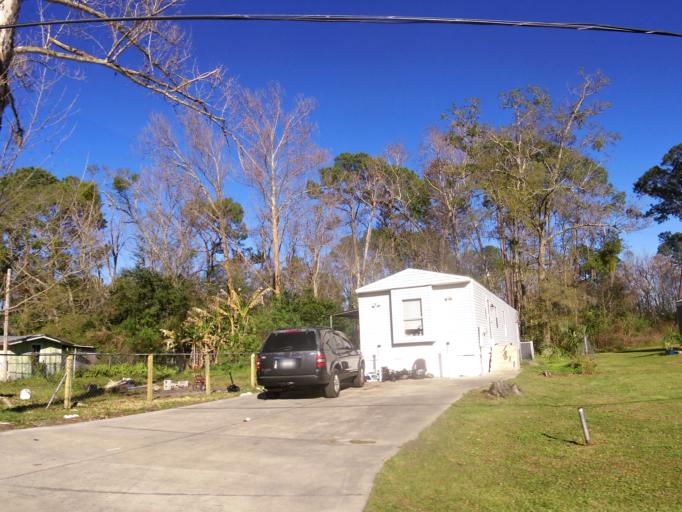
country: US
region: Florida
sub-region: Duval County
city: Jacksonville
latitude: 30.2750
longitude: -81.6285
